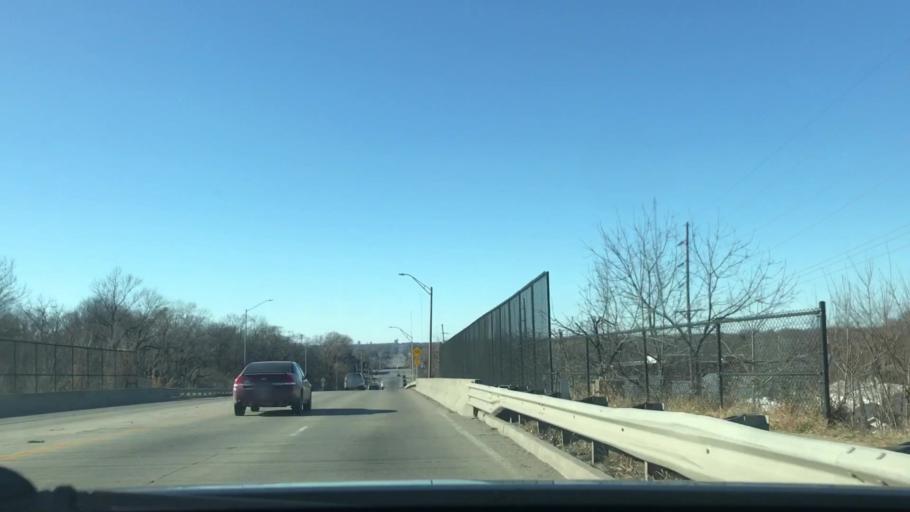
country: US
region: Missouri
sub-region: Jackson County
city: Independence
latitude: 39.0793
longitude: -94.4195
